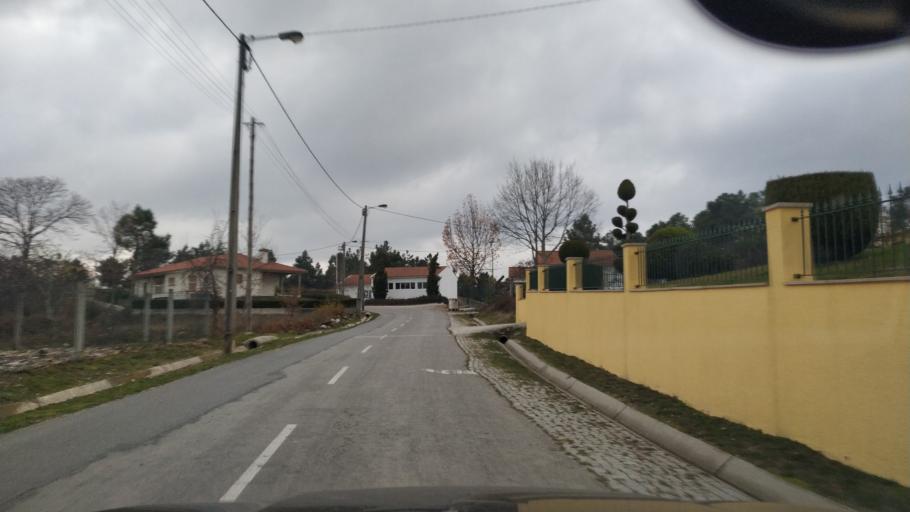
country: PT
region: Vila Real
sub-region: Sabrosa
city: Sabrosa
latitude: 41.3335
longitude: -7.6354
